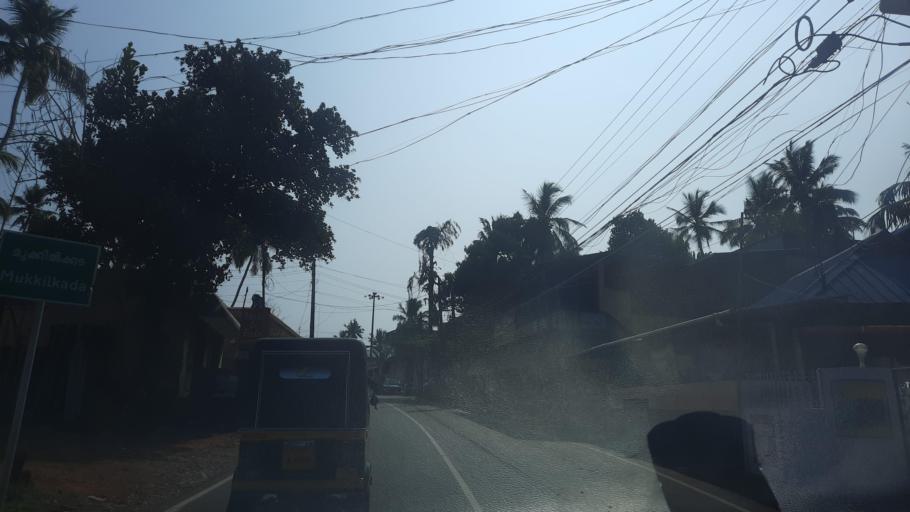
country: IN
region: Kerala
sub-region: Thiruvananthapuram
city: Nedumangad
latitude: 8.5710
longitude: 76.9240
